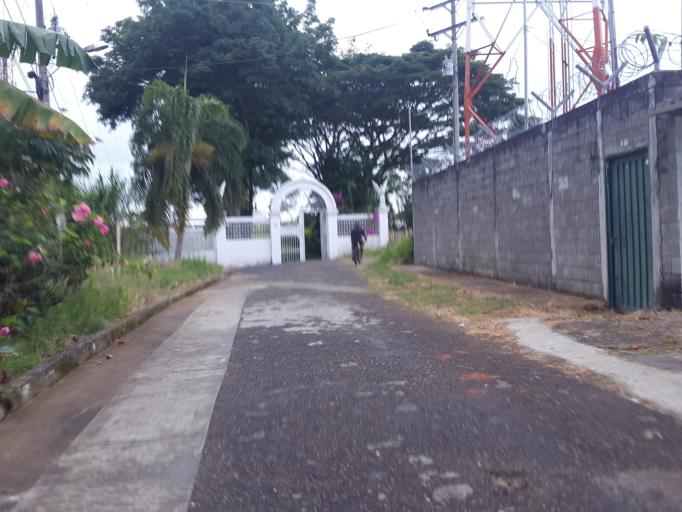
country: CO
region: Quindio
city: Buenavista
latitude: 4.3617
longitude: -75.7414
